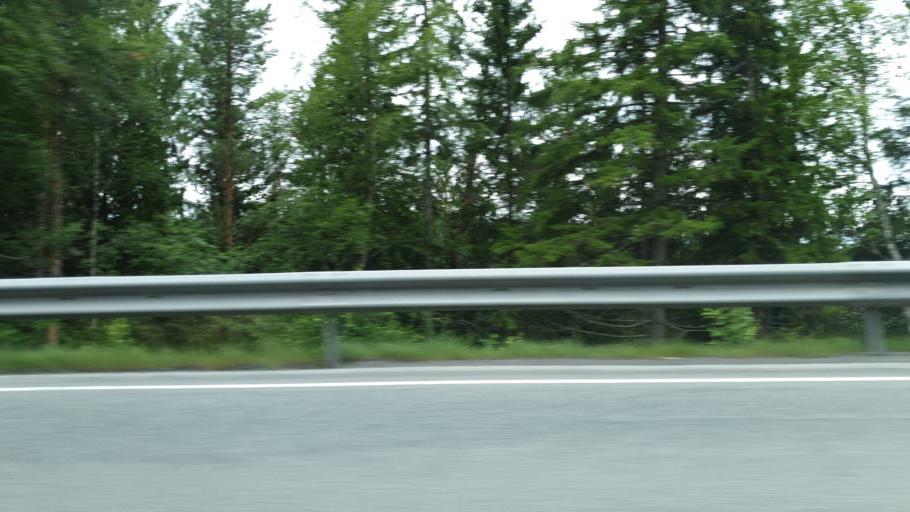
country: NO
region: Sor-Trondelag
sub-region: Rennebu
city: Berkak
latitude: 62.8118
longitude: 10.0311
